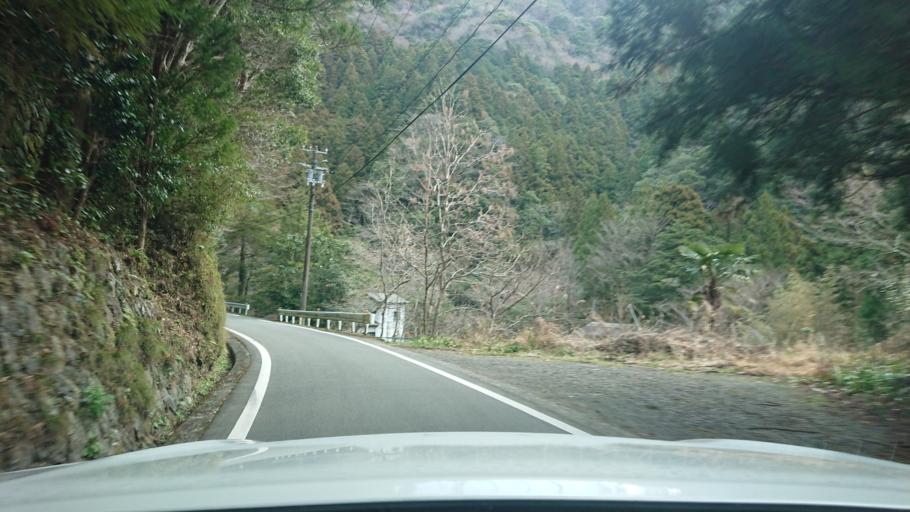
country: JP
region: Tokushima
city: Ishii
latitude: 33.9056
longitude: 134.3961
